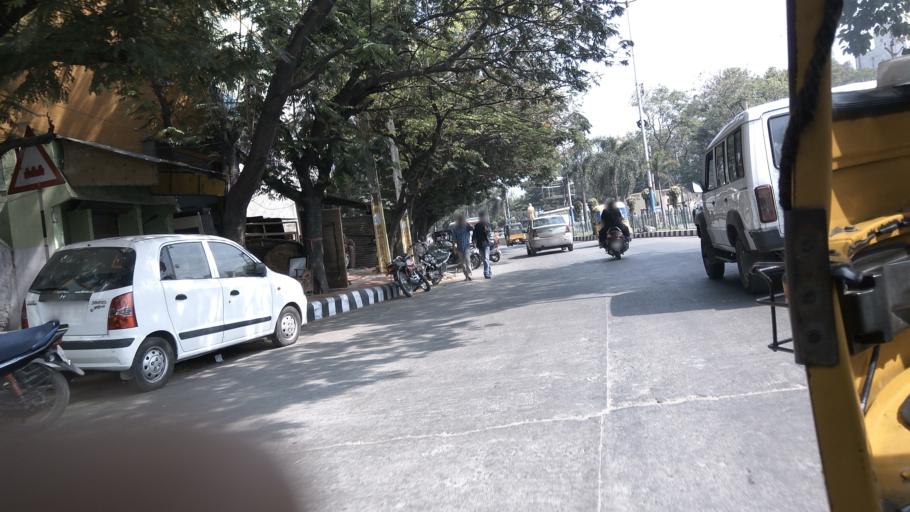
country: IN
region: Andhra Pradesh
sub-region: Chittoor
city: Tirupati
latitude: 13.6327
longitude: 79.4132
